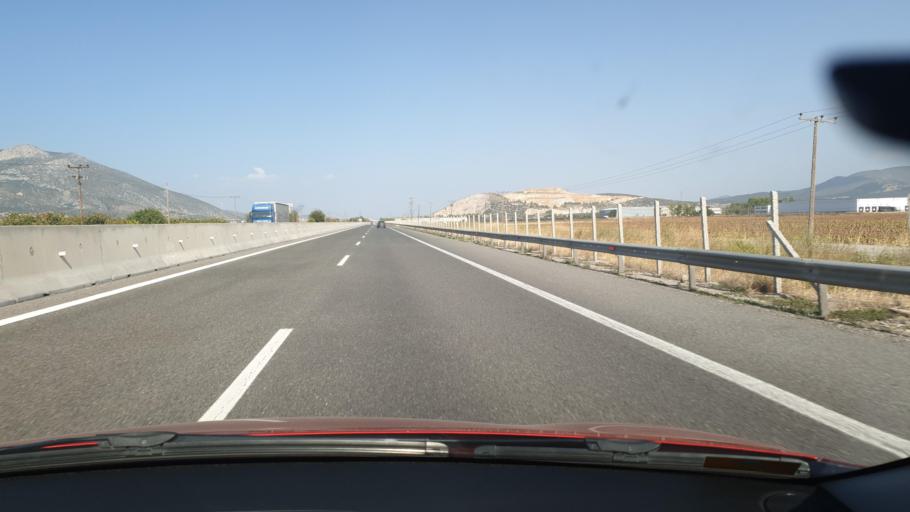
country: GR
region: Central Greece
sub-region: Nomos Voiotias
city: Thivai
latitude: 38.3678
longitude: 23.3567
